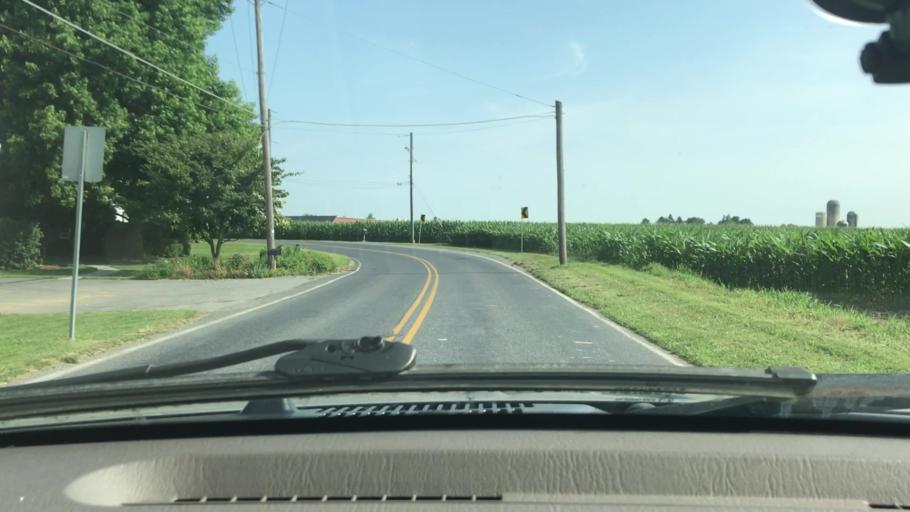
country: US
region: Pennsylvania
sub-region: Lancaster County
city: Rheems
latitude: 40.1602
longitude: -76.5717
